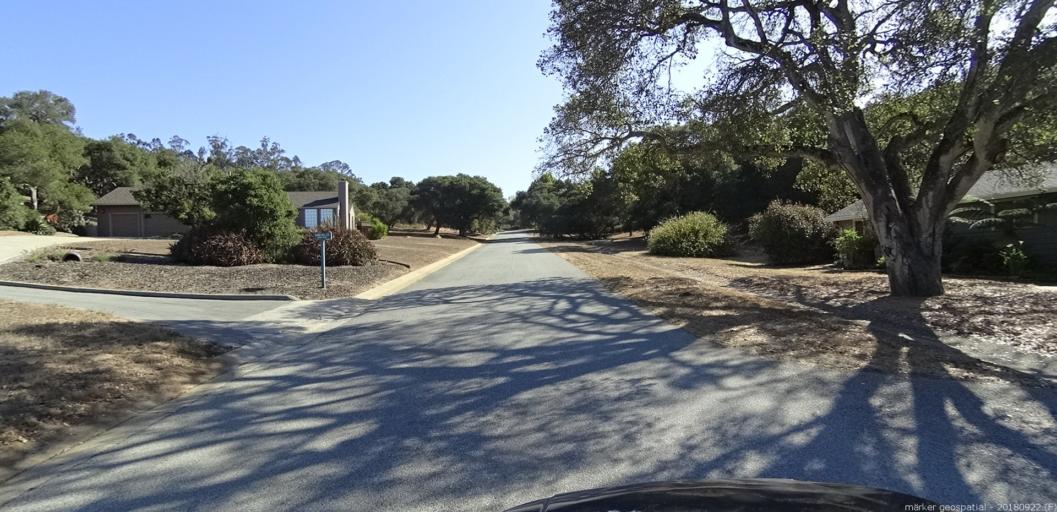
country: US
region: California
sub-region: Monterey County
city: Prunedale
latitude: 36.8063
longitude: -121.6577
